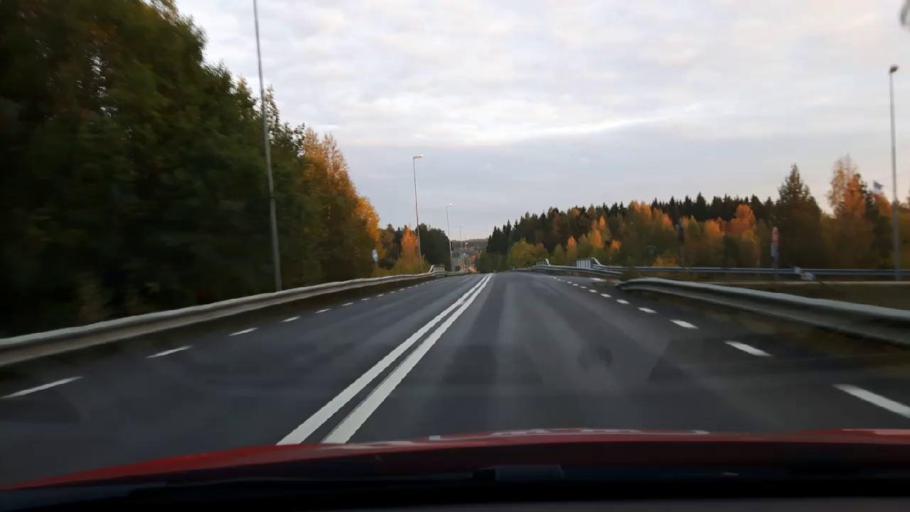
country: SE
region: Jaemtland
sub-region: OEstersunds Kommun
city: Lit
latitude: 63.3212
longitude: 14.8615
